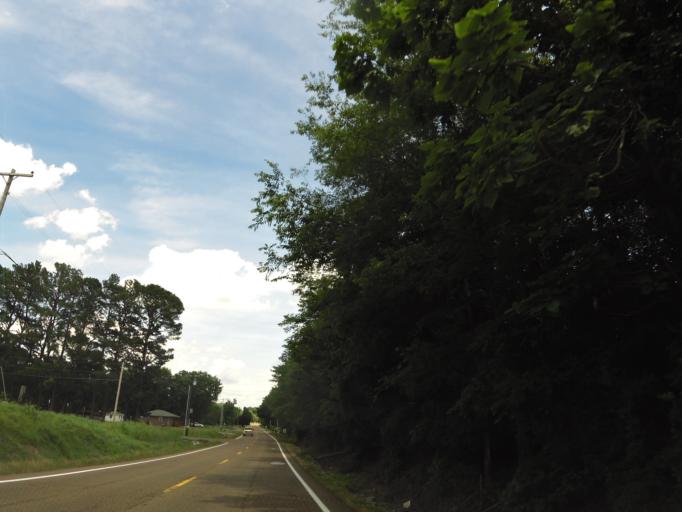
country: US
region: Tennessee
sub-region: Dyer County
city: Newbern
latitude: 36.0242
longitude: -89.2909
